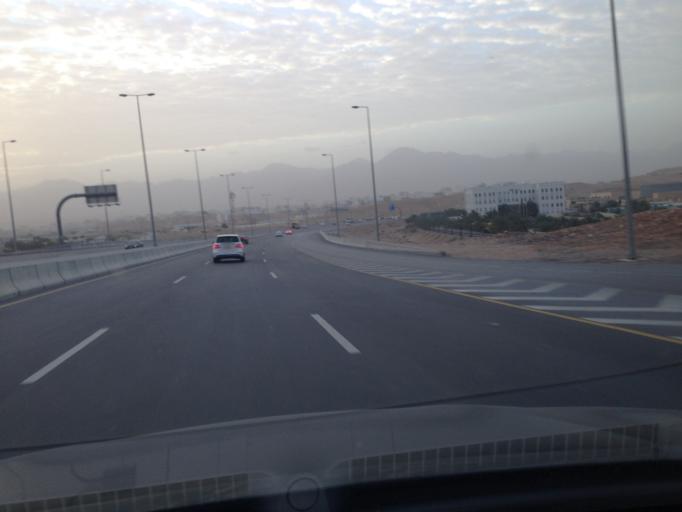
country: OM
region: Muhafazat Masqat
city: Bawshar
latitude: 23.5684
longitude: 58.3353
